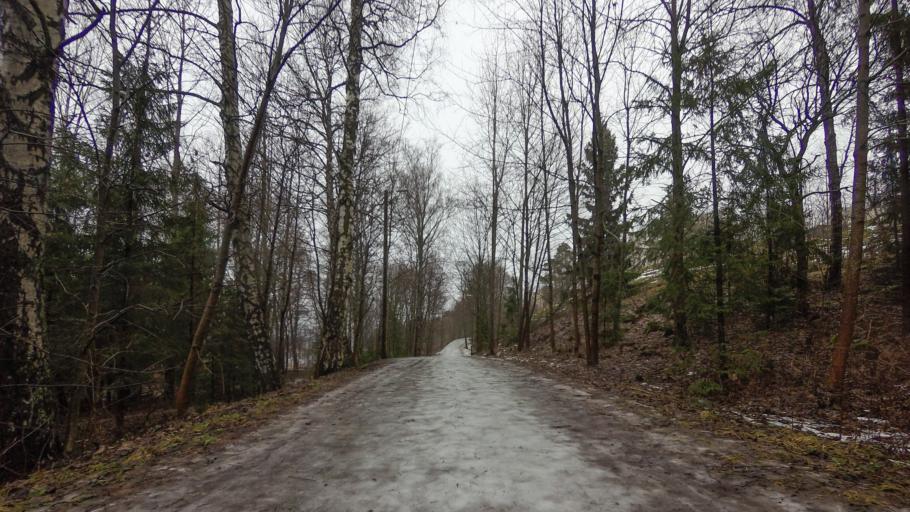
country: FI
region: Uusimaa
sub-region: Helsinki
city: Helsinki
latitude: 60.1936
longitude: 25.0236
